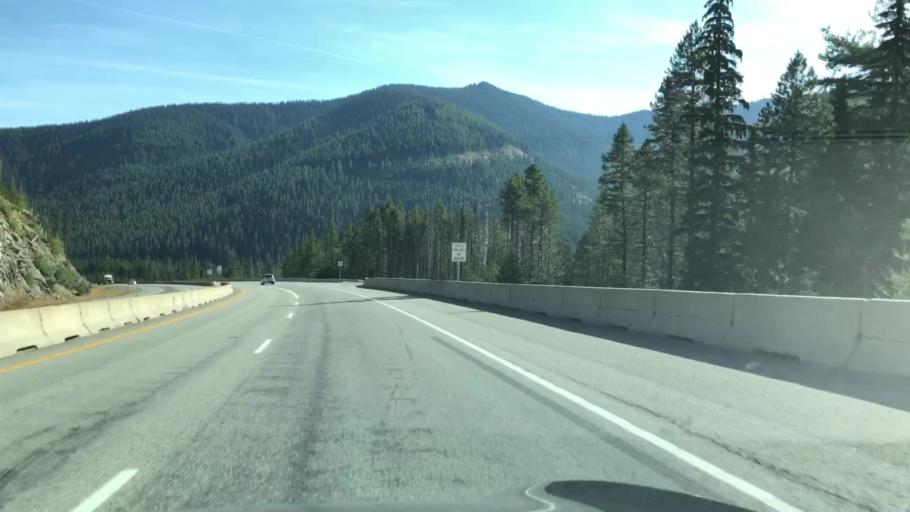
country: US
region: Idaho
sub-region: Shoshone County
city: Wallace
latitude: 47.4488
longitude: -115.6938
